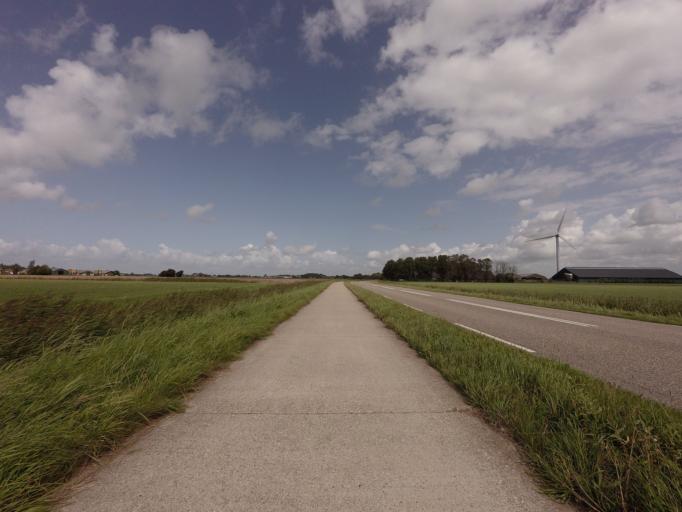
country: NL
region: Friesland
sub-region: Gemeente Harlingen
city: Harlingen
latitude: 53.1380
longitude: 5.4735
